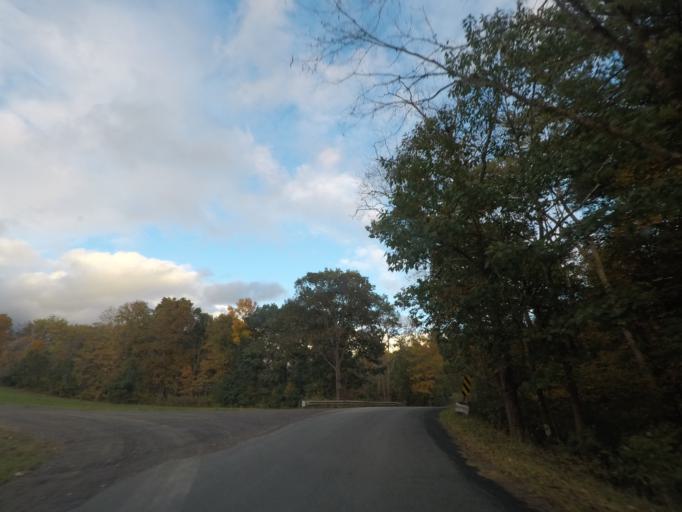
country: US
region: New York
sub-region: Rensselaer County
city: Nassau
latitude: 42.5451
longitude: -73.5832
